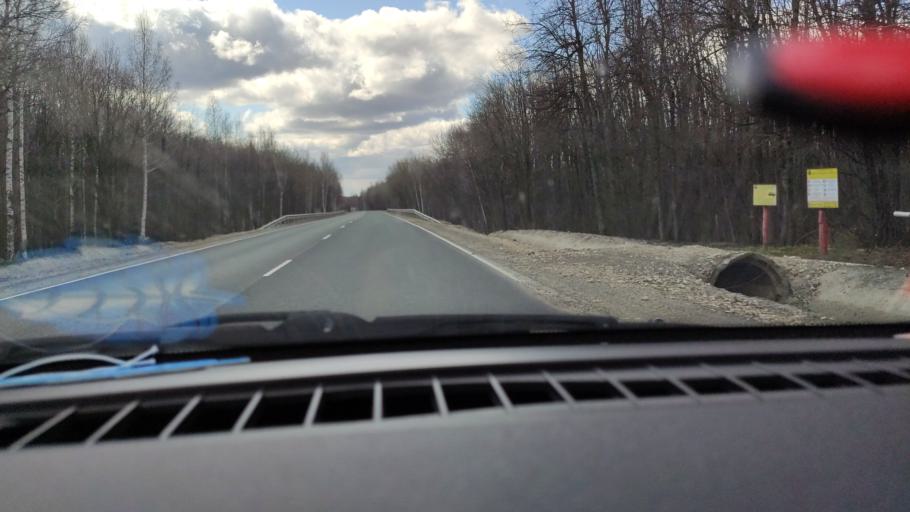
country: RU
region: Saratov
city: Khvalynsk
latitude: 52.4449
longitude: 48.0099
